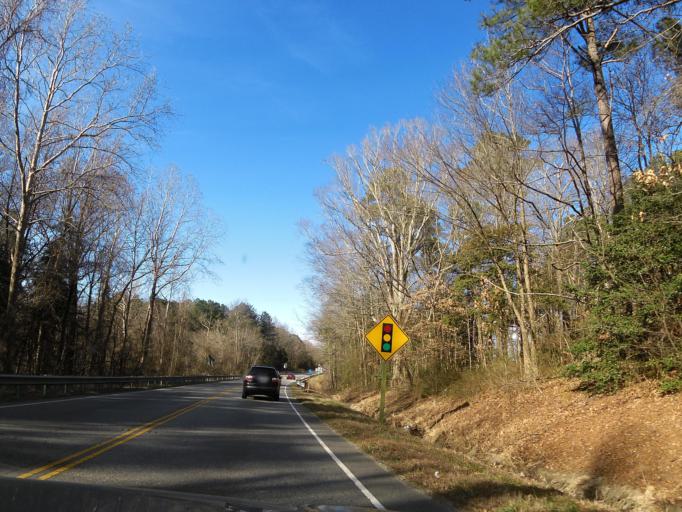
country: US
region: Virginia
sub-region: Isle of Wight County
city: Smithfield
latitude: 36.9737
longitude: -76.6382
